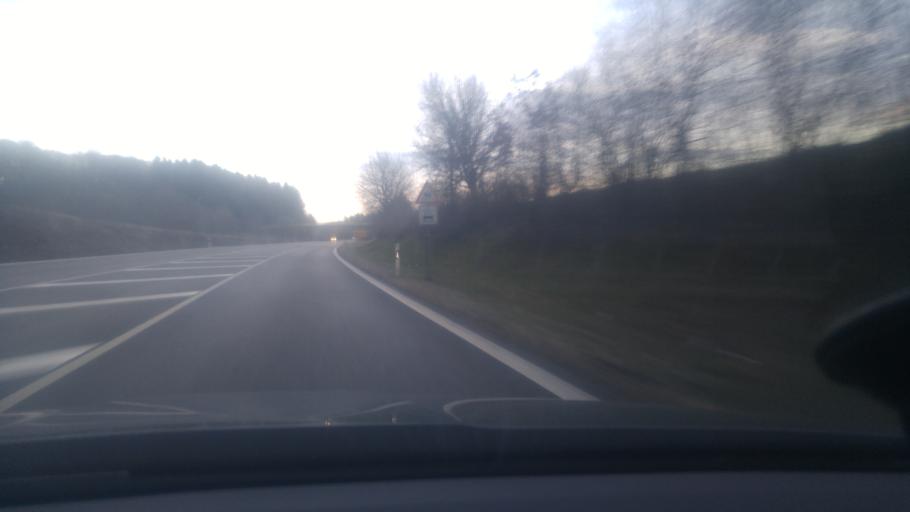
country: DE
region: Baden-Wuerttemberg
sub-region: Freiburg Region
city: Lauchringen
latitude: 47.6362
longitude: 8.3144
